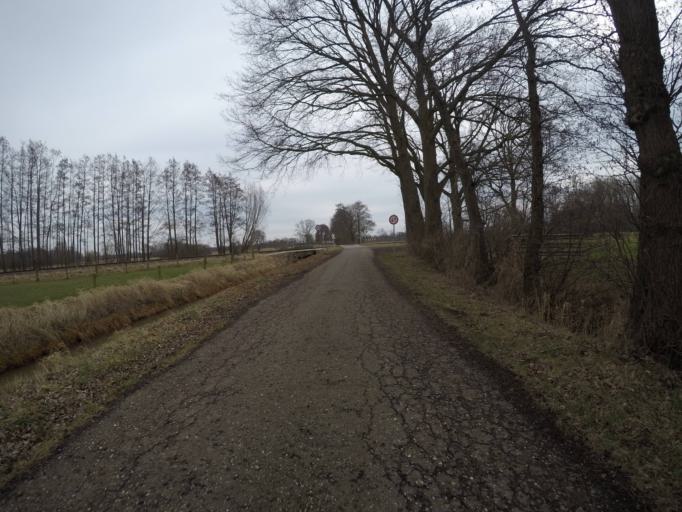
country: DE
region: North Rhine-Westphalia
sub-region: Regierungsbezirk Dusseldorf
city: Hamminkeln
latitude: 51.7509
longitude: 6.6060
